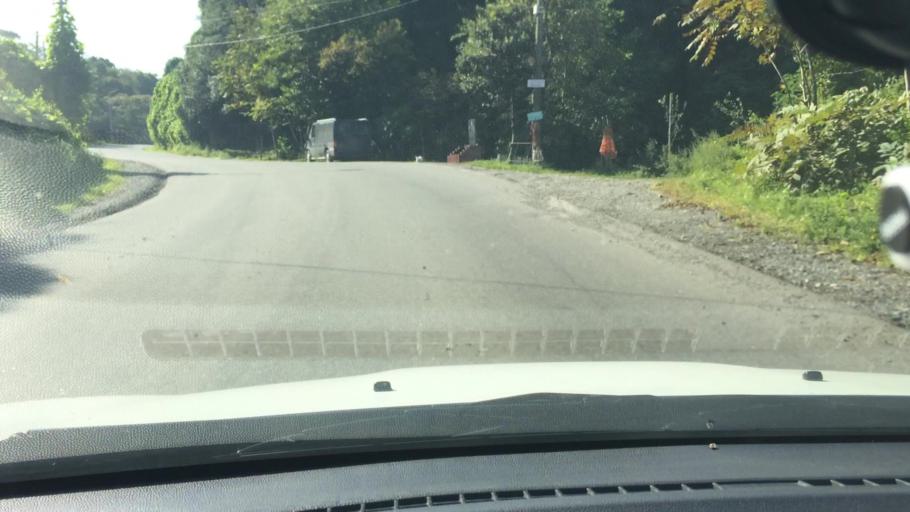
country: GE
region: Ajaria
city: Kobuleti
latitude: 41.7692
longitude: 41.7550
